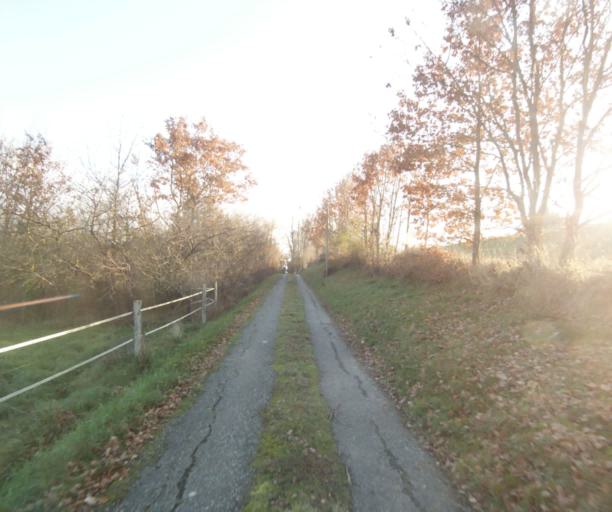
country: FR
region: Midi-Pyrenees
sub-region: Departement du Tarn-et-Garonne
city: Moissac
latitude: 44.1249
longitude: 1.1306
